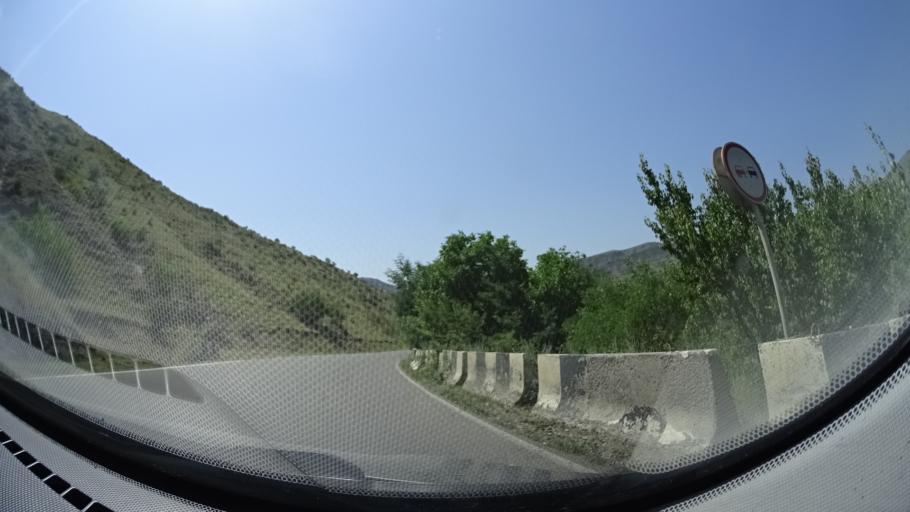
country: GE
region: Samtskhe-Javakheti
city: Aspindza
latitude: 41.5152
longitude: 43.2614
